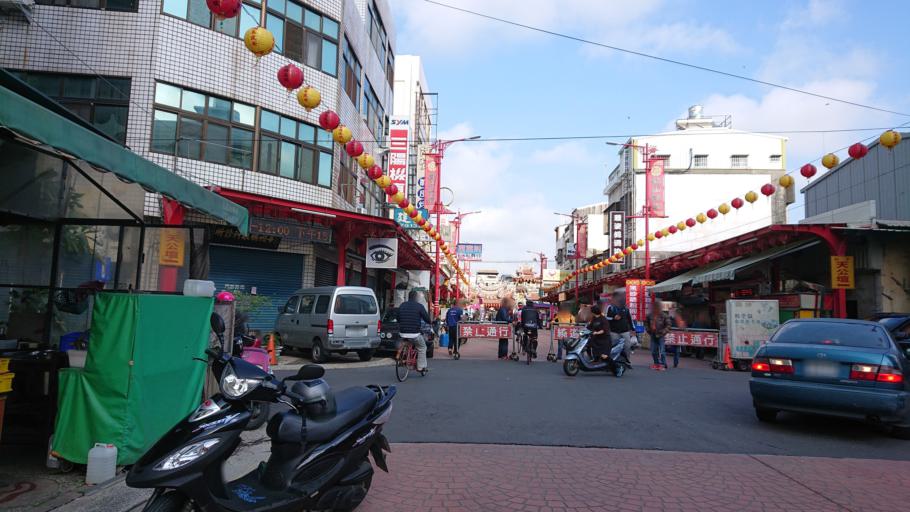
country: TW
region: Taiwan
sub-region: Chiayi
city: Taibao
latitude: 23.4669
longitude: 120.2458
